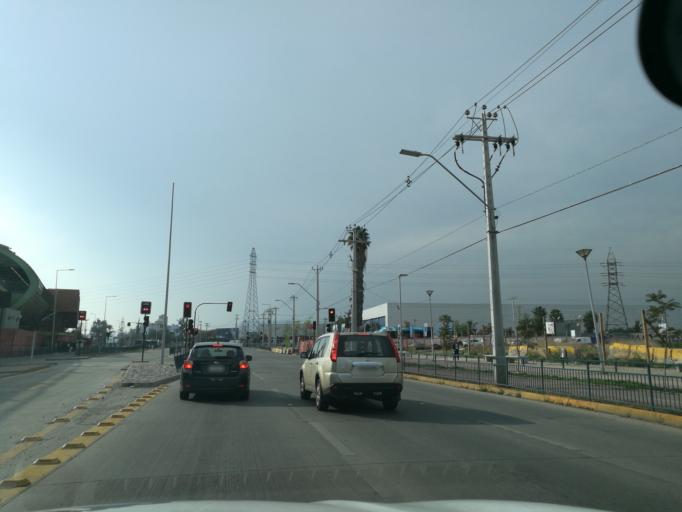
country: CL
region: Santiago Metropolitan
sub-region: Provincia de Santiago
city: Santiago
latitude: -33.4876
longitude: -70.6182
